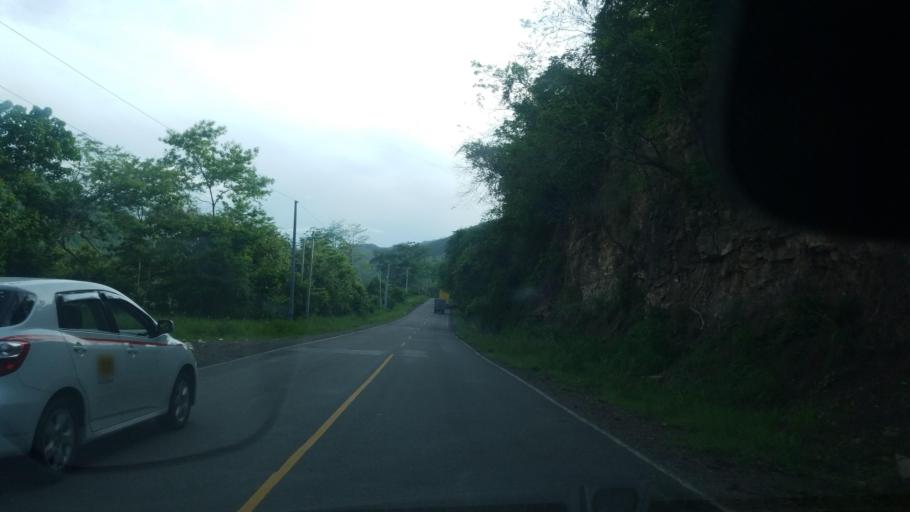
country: HN
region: Santa Barbara
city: Ilama
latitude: 15.0903
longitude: -88.2097
